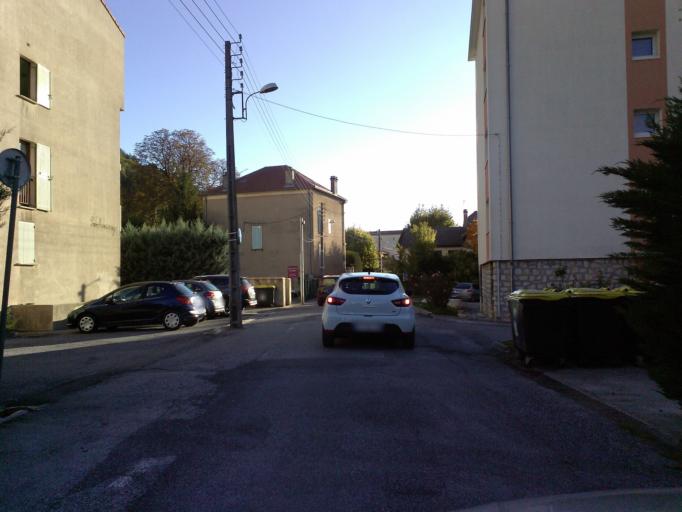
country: FR
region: Provence-Alpes-Cote d'Azur
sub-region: Departement des Alpes-de-Haute-Provence
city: Digne-les-Bains
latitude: 44.0874
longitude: 6.2300
